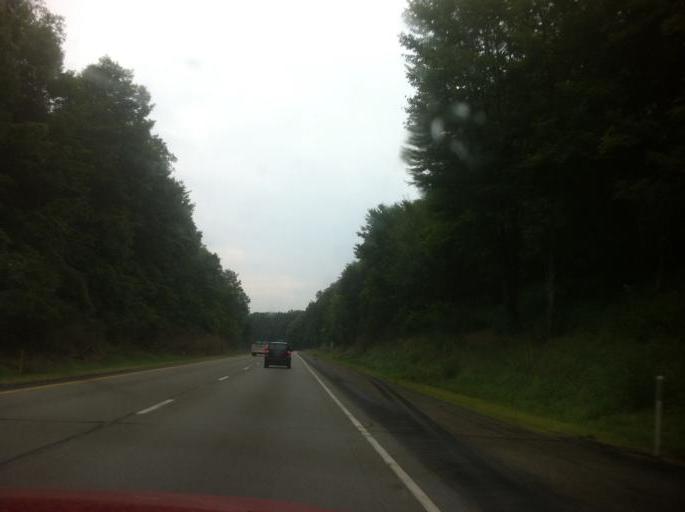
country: US
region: Pennsylvania
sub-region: Clarion County
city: Clarion
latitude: 41.1812
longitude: -79.3148
